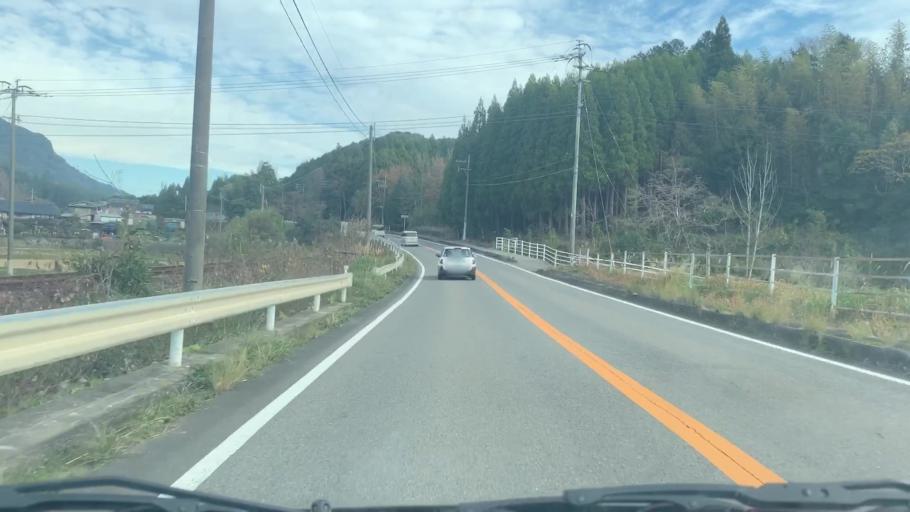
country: JP
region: Saga Prefecture
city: Karatsu
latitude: 33.3387
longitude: 129.9798
